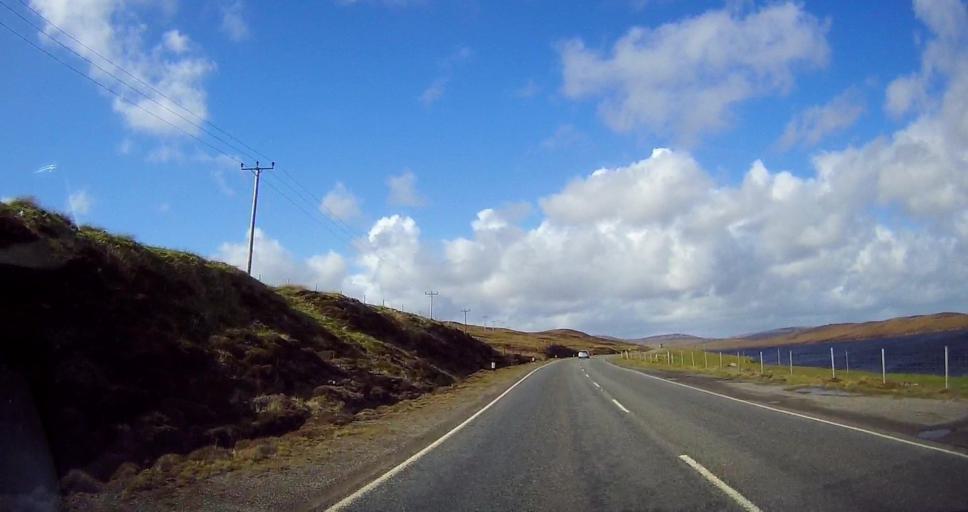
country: GB
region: Scotland
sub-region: Shetland Islands
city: Lerwick
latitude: 60.2446
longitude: -1.2287
